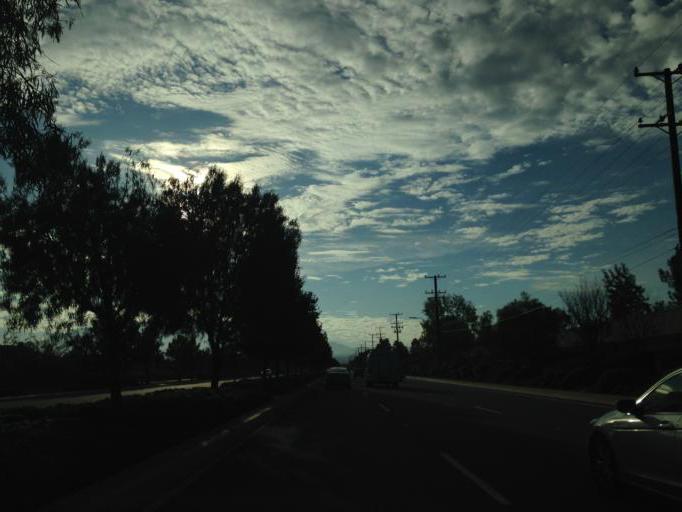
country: US
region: California
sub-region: Riverside County
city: Temecula
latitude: 33.4648
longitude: -117.1147
